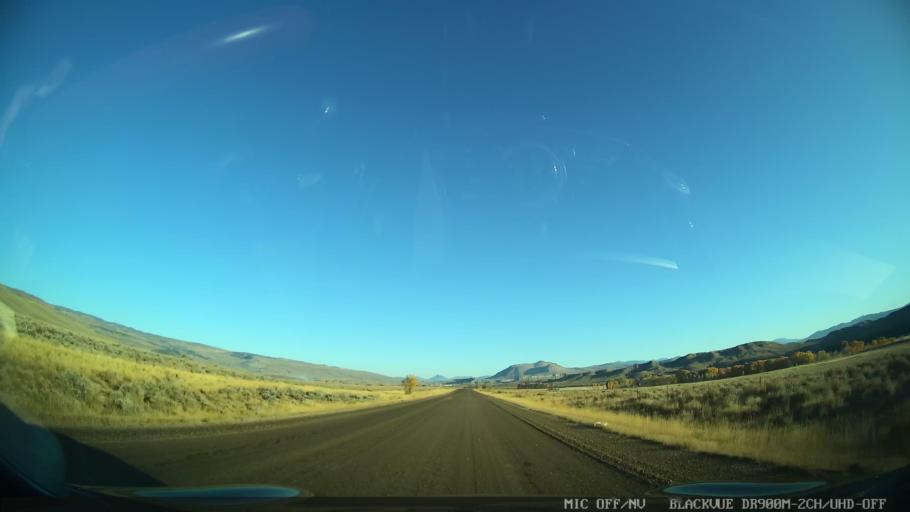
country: US
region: Colorado
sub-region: Grand County
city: Kremmling
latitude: 40.0218
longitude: -106.3892
